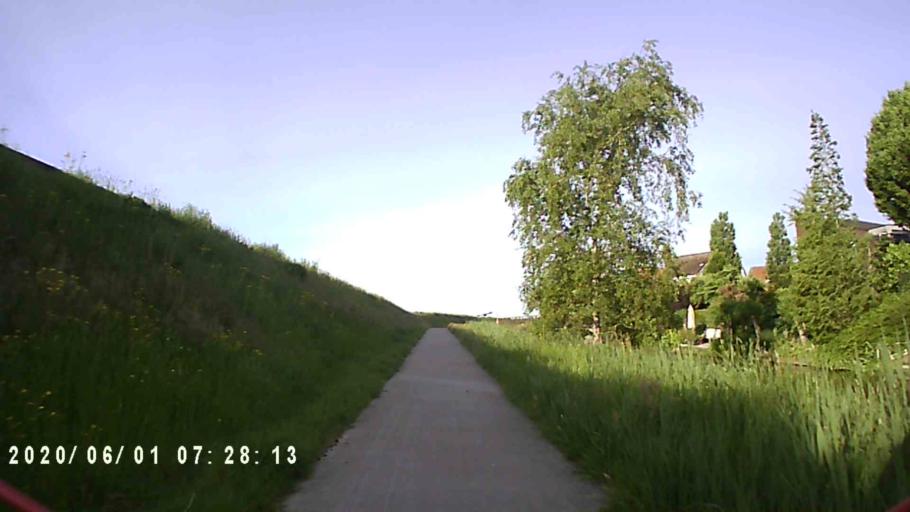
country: NL
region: Friesland
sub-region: Gemeente Dongeradeel
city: Dokkum
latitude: 53.3151
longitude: 6.0156
